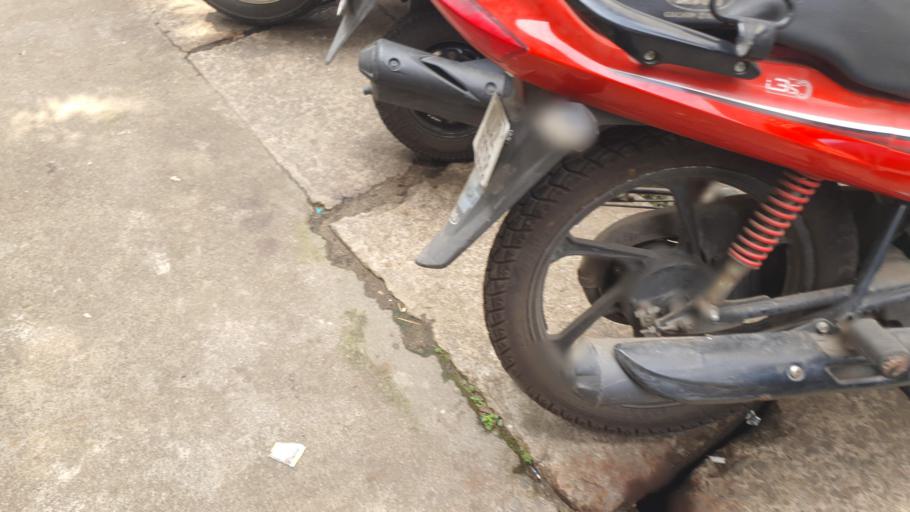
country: IN
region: Kerala
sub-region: Ernakulam
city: Cochin
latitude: 9.9951
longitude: 76.2911
